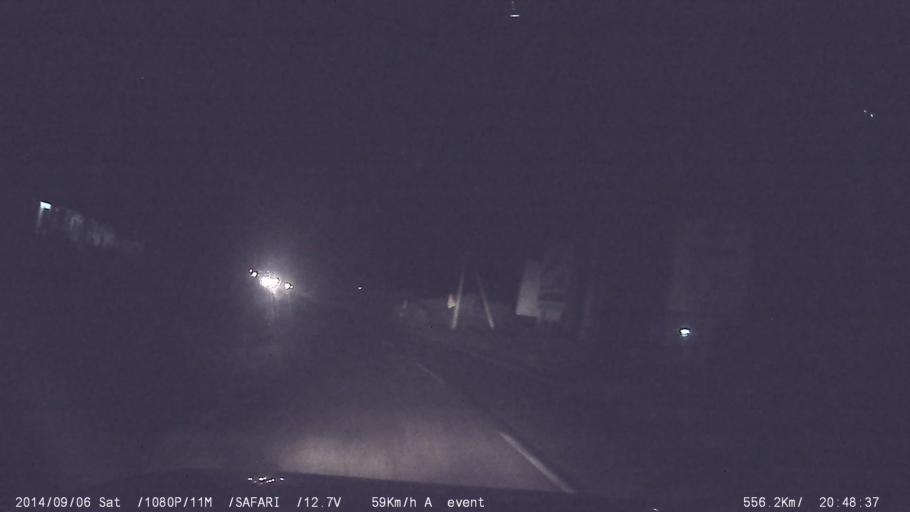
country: IN
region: Kerala
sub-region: Kottayam
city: Palackattumala
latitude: 9.7322
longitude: 76.5614
